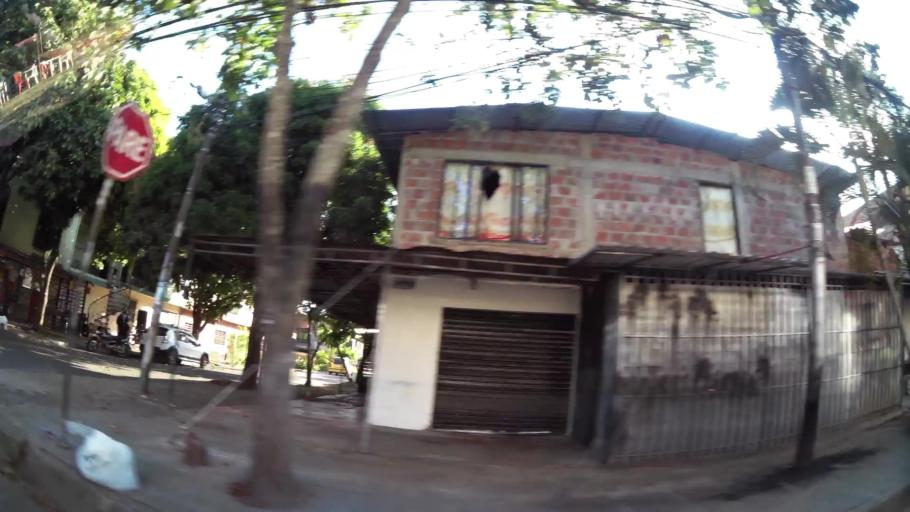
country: CO
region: Valle del Cauca
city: Cali
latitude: 3.4129
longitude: -76.5133
